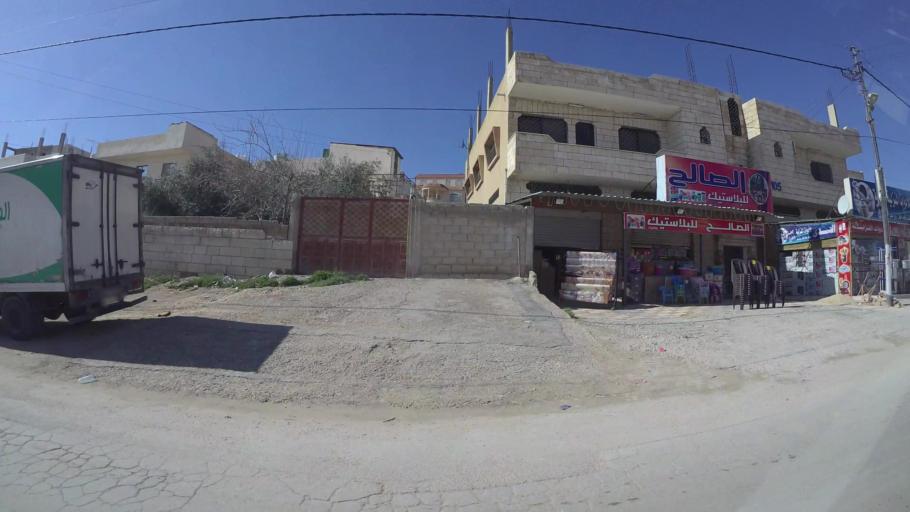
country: JO
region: Zarqa
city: Russeifa
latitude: 32.0383
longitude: 36.0504
